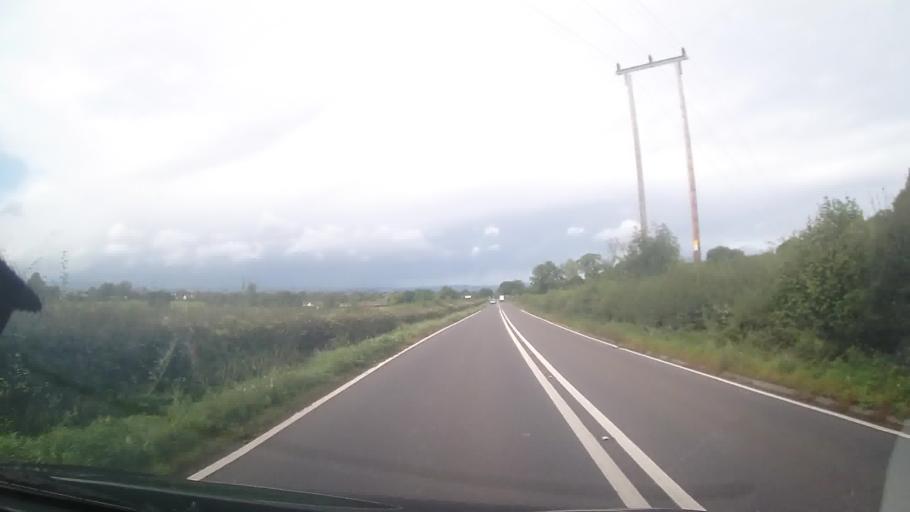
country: GB
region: England
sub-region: Shropshire
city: Romsley
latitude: 52.4397
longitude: -2.3292
